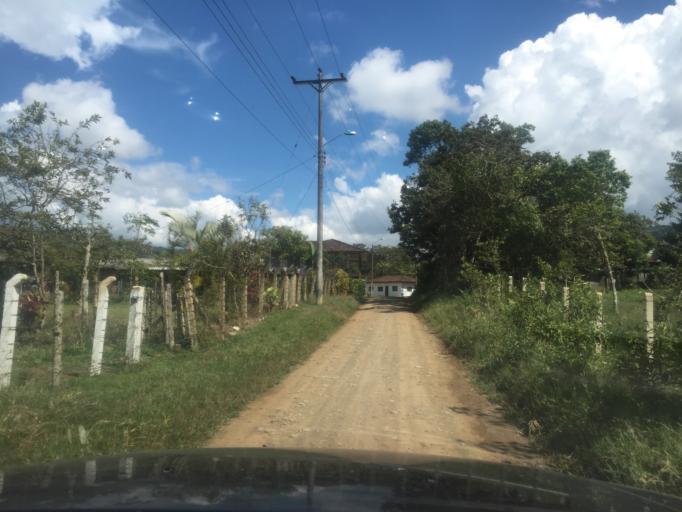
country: CO
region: Valle del Cauca
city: Yumbo
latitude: 3.6603
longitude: -76.5583
